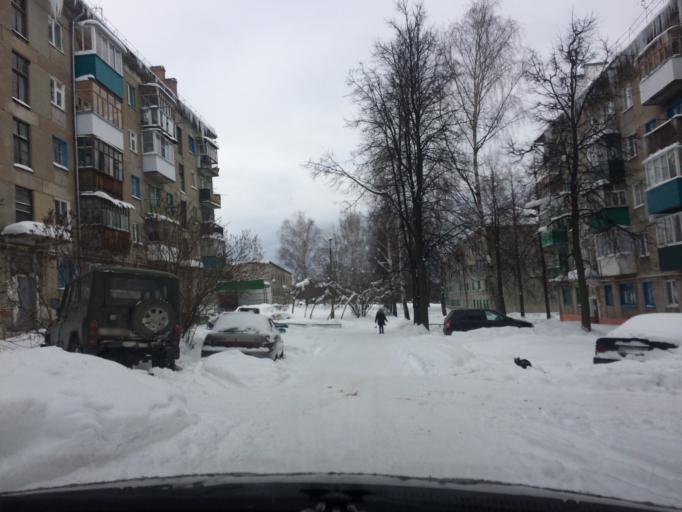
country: RU
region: Mariy-El
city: Mochalishche
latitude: 56.5445
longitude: 48.4037
